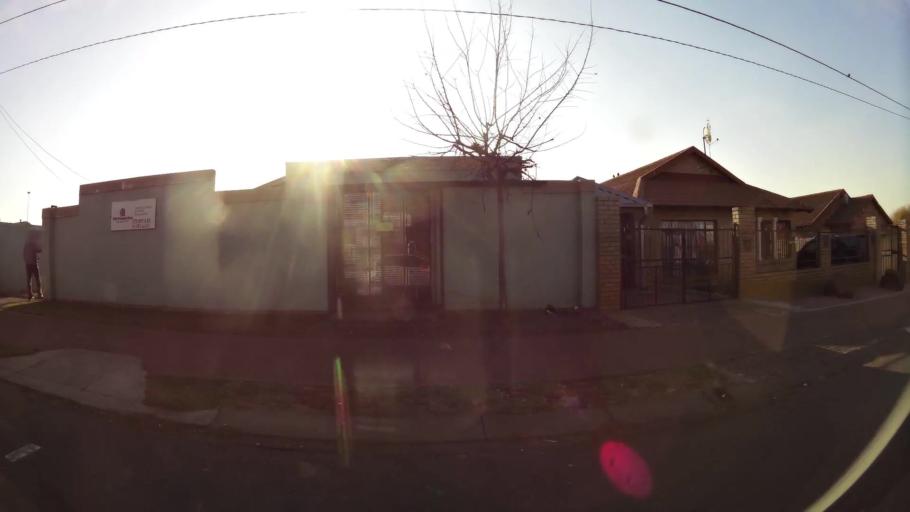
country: ZA
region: Gauteng
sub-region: City of Johannesburg Metropolitan Municipality
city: Soweto
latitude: -26.2638
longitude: 27.8767
